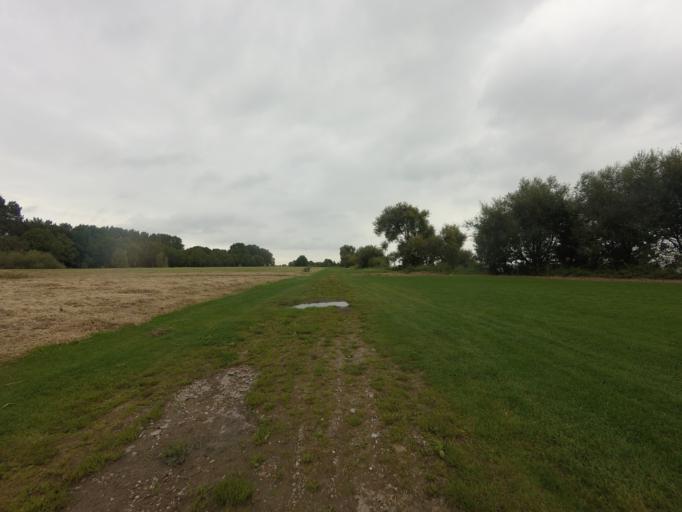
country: NL
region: North Holland
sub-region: Gemeente Enkhuizen
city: Enkhuizen
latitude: 52.7148
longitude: 5.2875
